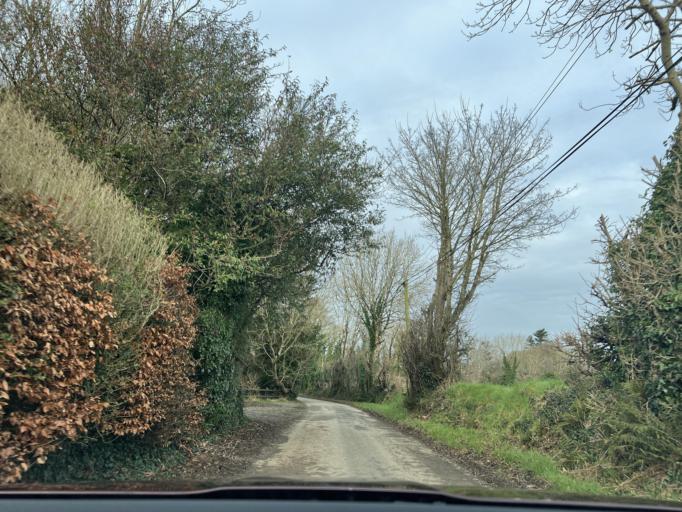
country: IE
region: Leinster
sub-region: Loch Garman
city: Loch Garman
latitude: 52.3650
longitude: -6.5312
